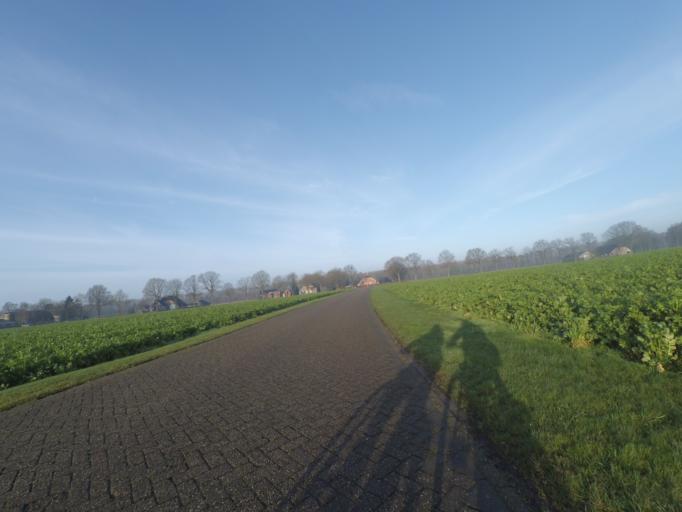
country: NL
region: Drenthe
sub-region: Gemeente Borger-Odoorn
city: Borger
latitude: 52.9060
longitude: 6.7731
